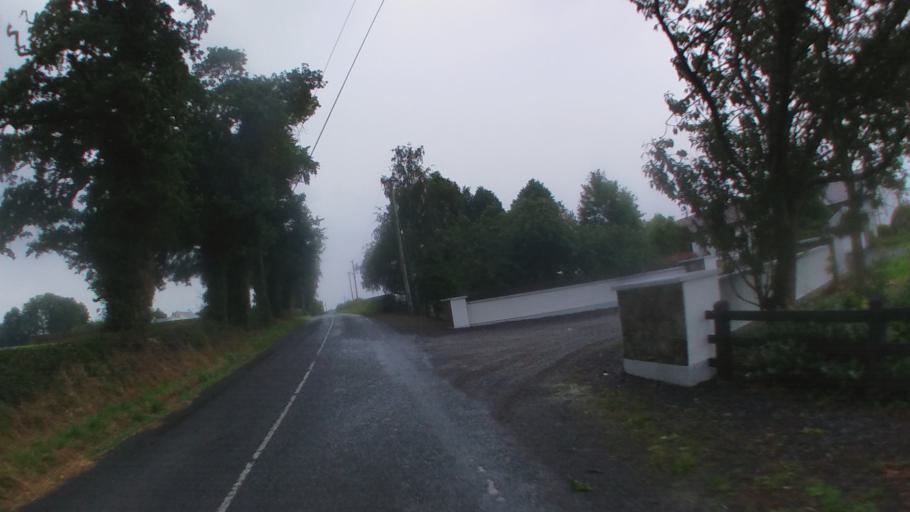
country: IE
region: Leinster
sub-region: Kilkenny
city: Callan
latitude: 52.5115
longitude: -7.4836
